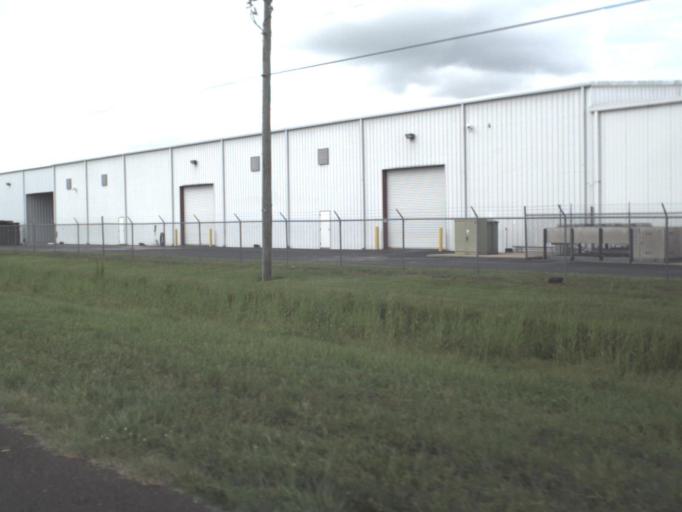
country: US
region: Florida
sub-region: Hillsborough County
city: Plant City
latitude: 27.9514
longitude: -82.1213
